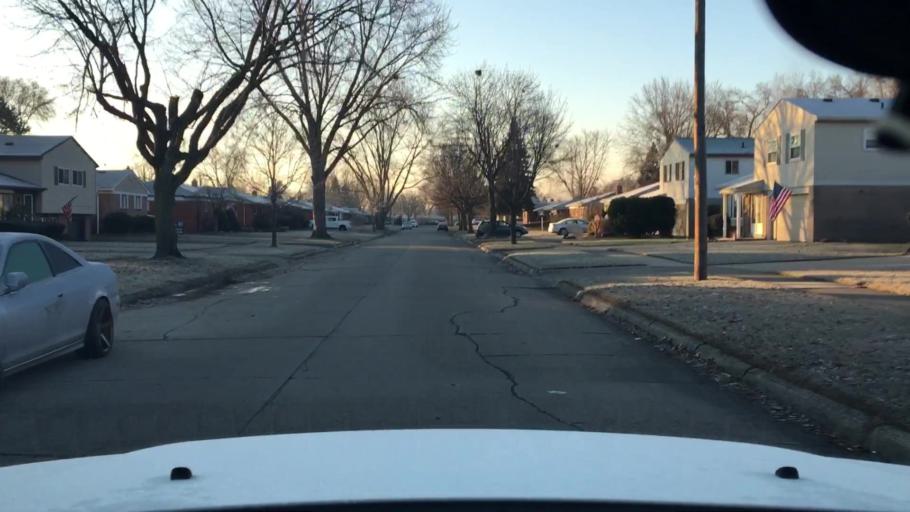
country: US
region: Michigan
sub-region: Oakland County
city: Madison Heights
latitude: 42.4862
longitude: -83.0721
